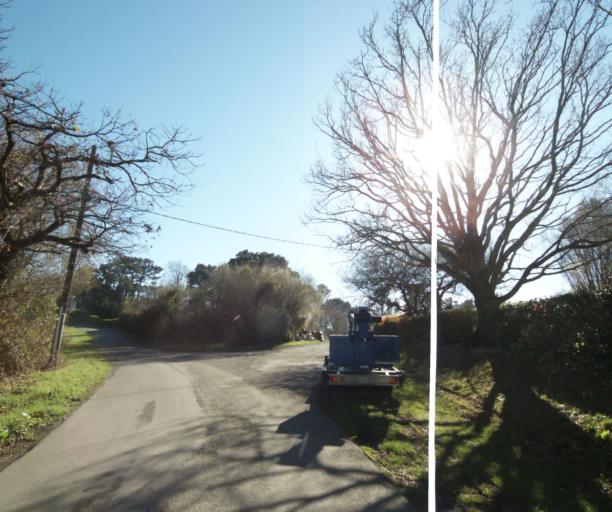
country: FR
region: Aquitaine
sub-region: Departement des Pyrenees-Atlantiques
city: Urrugne
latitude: 43.3684
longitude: -1.7356
